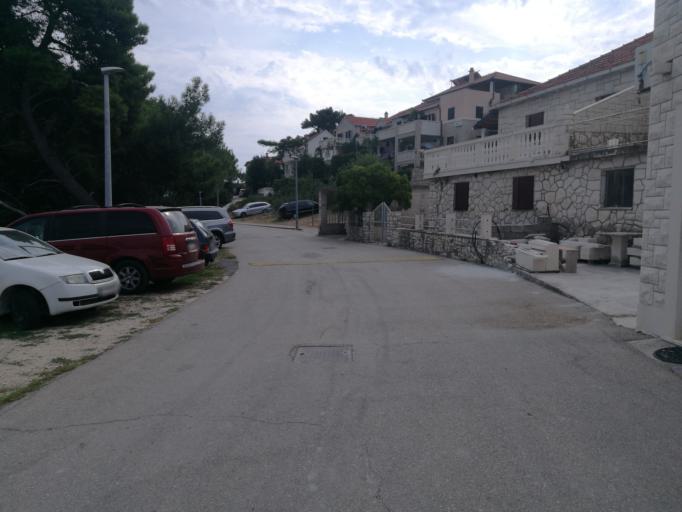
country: HR
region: Splitsko-Dalmatinska
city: Postira
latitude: 43.3764
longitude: 16.6347
